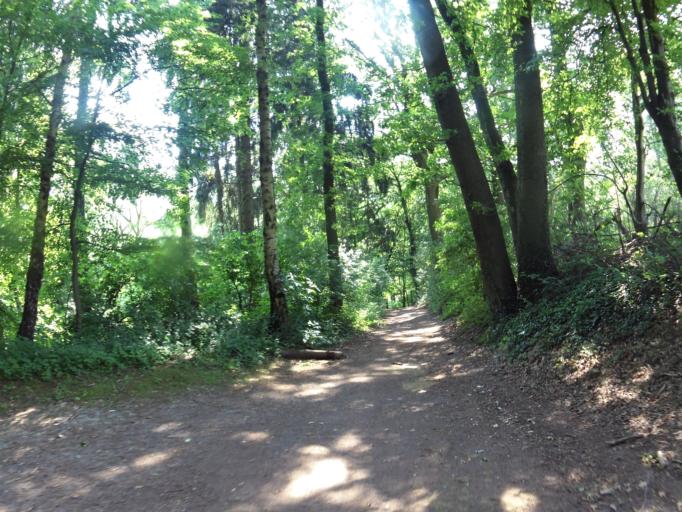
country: DE
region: North Rhine-Westphalia
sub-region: Regierungsbezirk Koln
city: Wurselen
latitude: 50.8120
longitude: 6.1036
